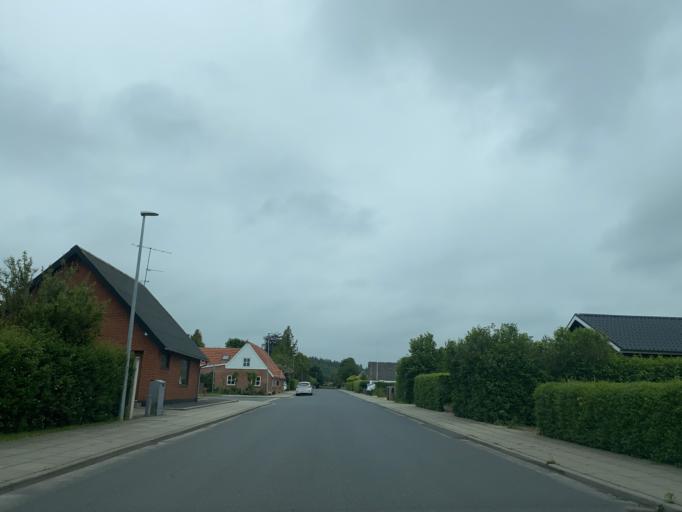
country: DK
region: Central Jutland
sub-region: Viborg Kommune
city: Bjerringbro
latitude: 56.3657
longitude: 9.6570
